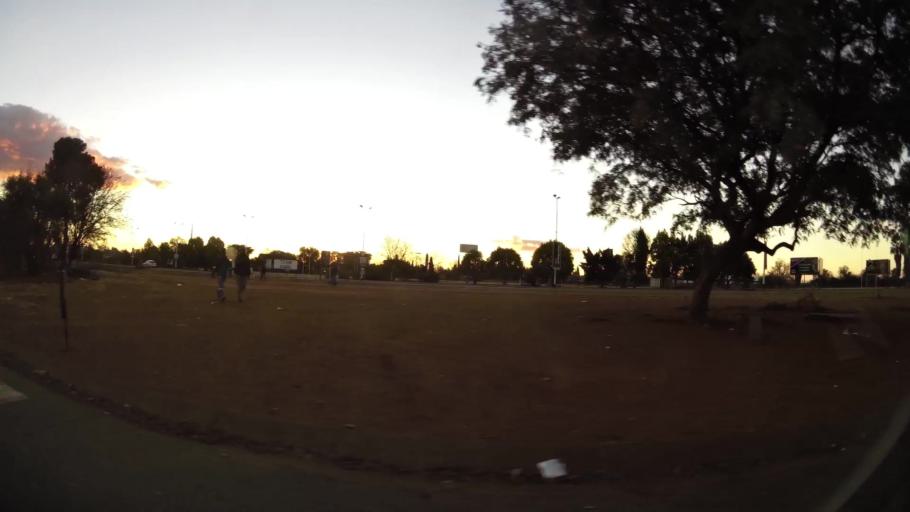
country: ZA
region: North-West
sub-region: Dr Kenneth Kaunda District Municipality
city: Potchefstroom
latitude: -26.7088
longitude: 27.1169
